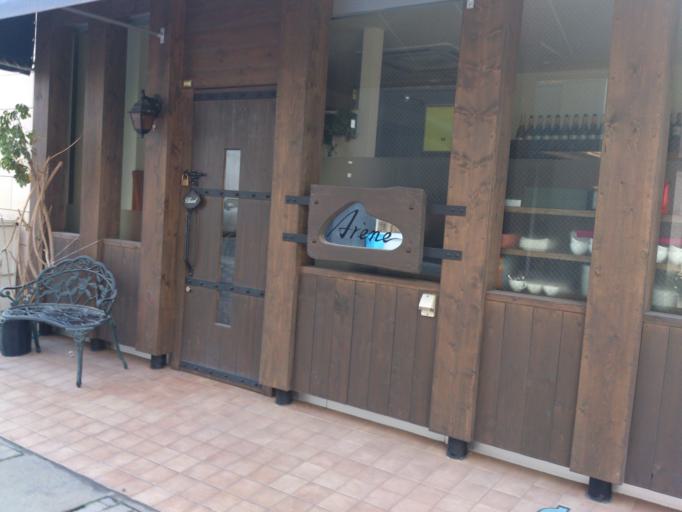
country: JP
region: Kagoshima
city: Kagoshima-shi
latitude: 31.5812
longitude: 130.5423
